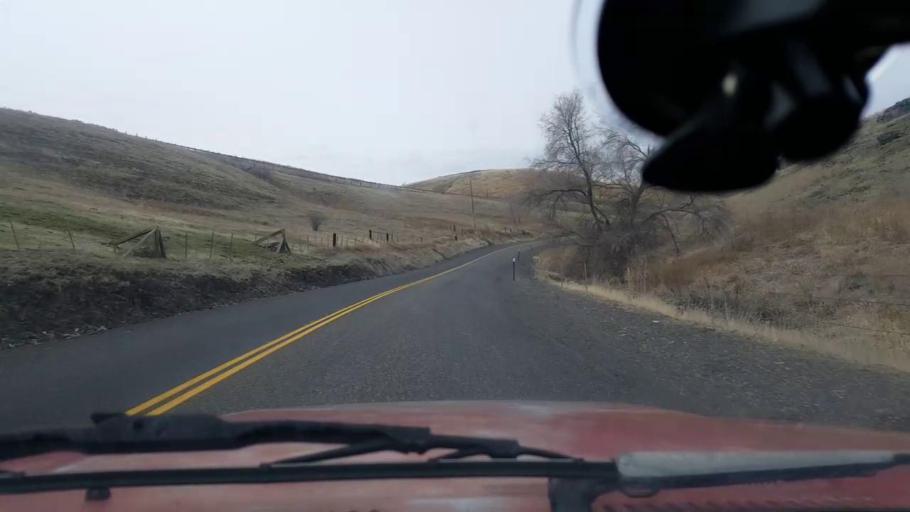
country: US
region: Washington
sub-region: Asotin County
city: Clarkston Heights-Vineland
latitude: 46.3836
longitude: -117.1351
